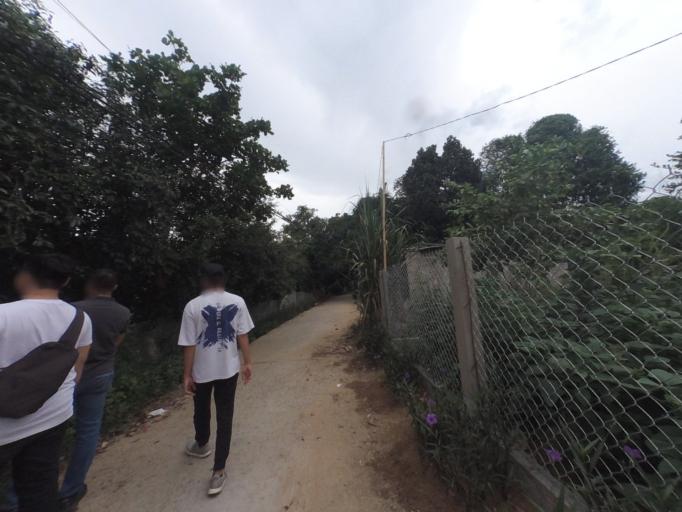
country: VN
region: Thua Thien-Hue
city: A Luoi
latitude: 16.2974
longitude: 107.3519
